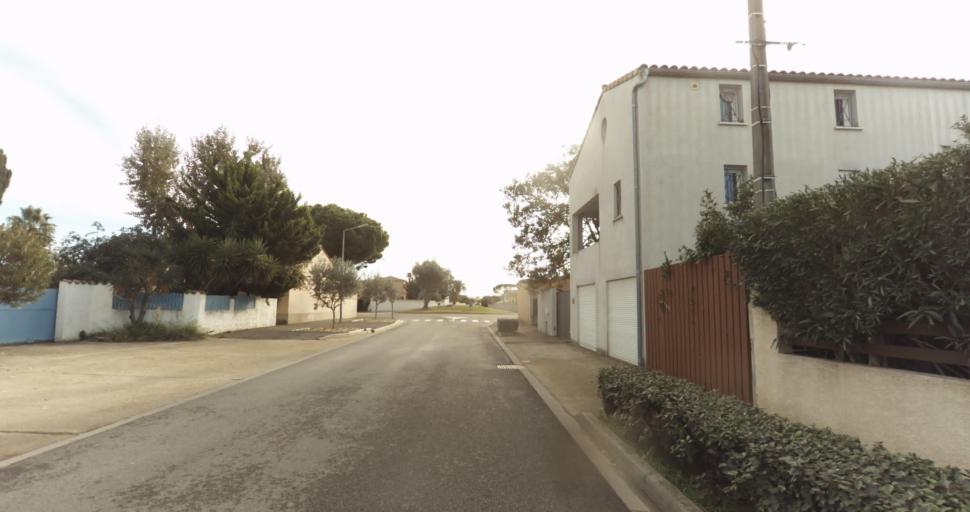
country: FR
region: Languedoc-Roussillon
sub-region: Departement du Gard
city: Aigues-Mortes
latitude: 43.5670
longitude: 4.2025
